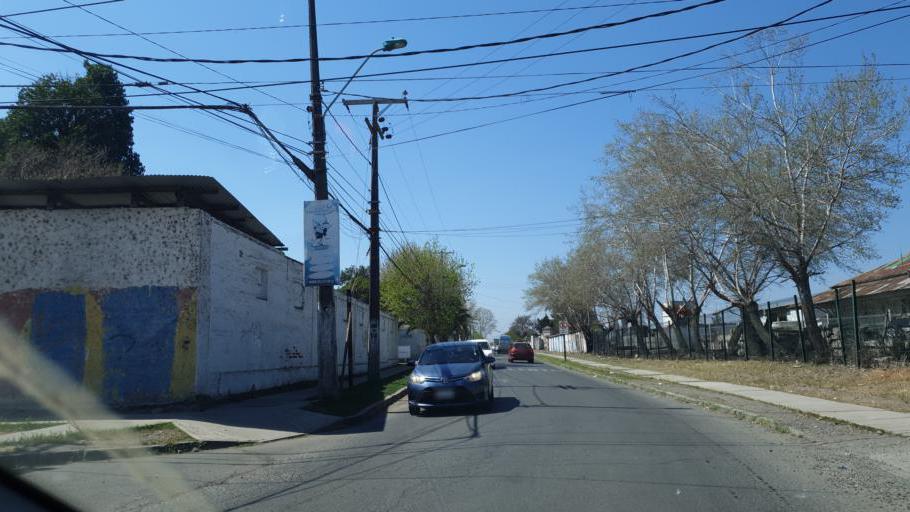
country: CL
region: Santiago Metropolitan
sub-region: Provincia de Talagante
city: Talagante
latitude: -33.6588
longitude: -70.9277
